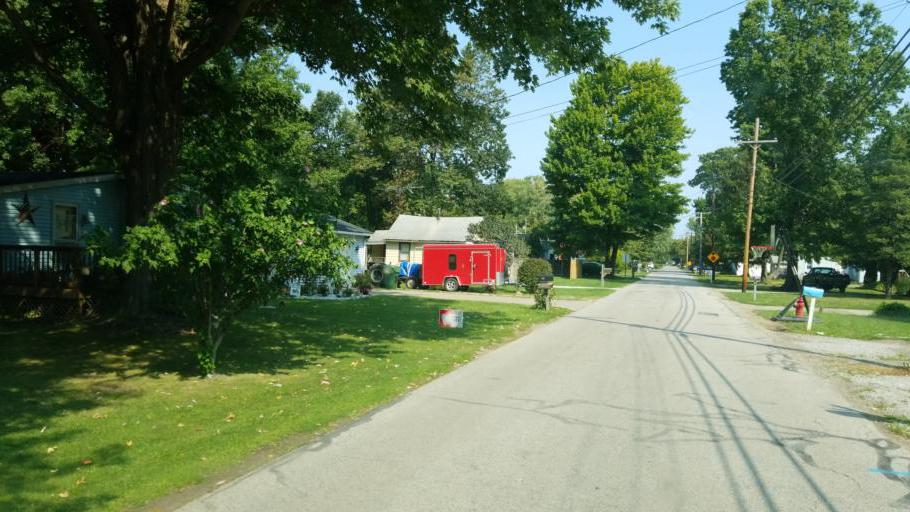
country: US
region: Ohio
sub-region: Lake County
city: Painesville
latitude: 41.7627
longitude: -81.2248
